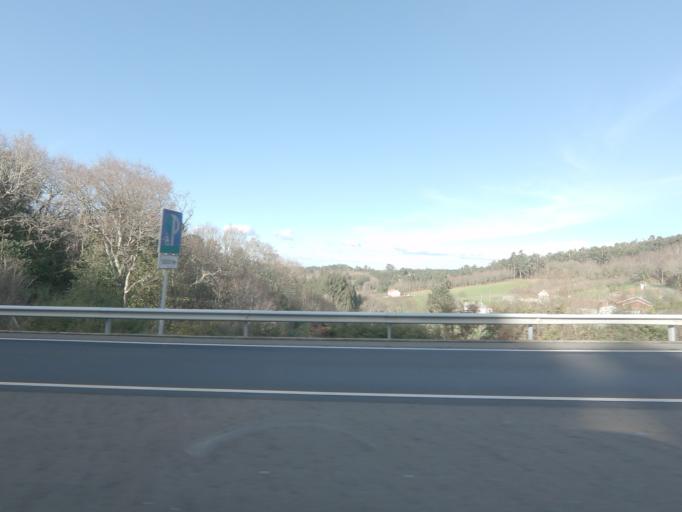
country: ES
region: Galicia
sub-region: Provincia da Coruna
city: Ribeira
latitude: 42.7131
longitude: -8.3709
